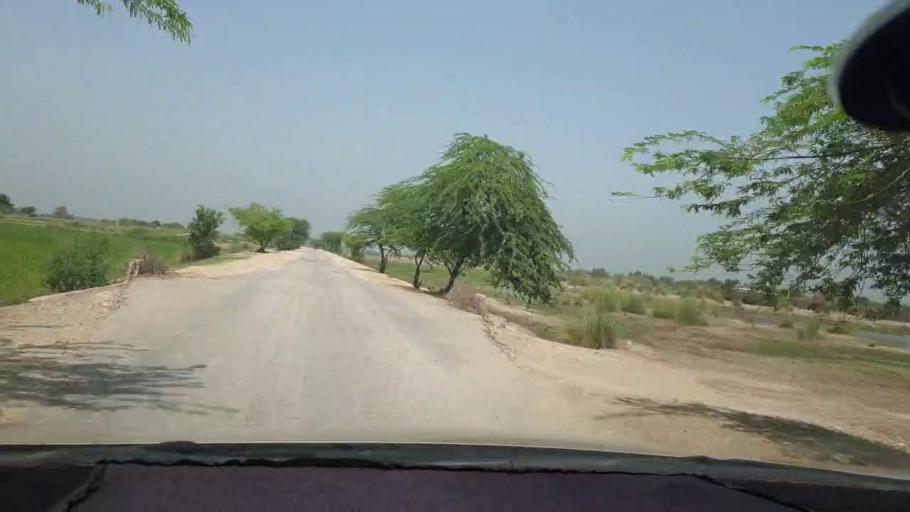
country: PK
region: Sindh
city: Kambar
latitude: 27.6710
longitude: 67.9126
